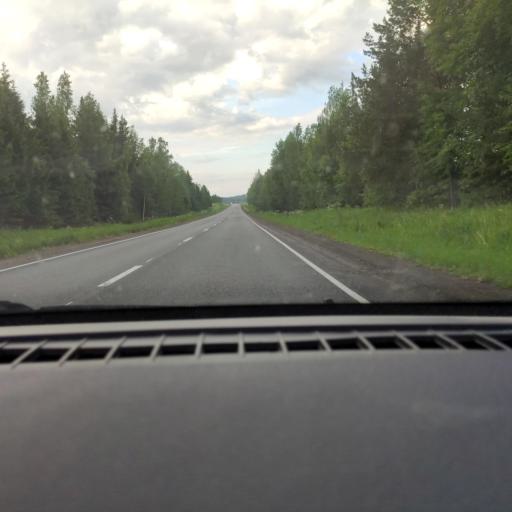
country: RU
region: Udmurtiya
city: Votkinsk
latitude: 57.2029
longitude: 54.1612
